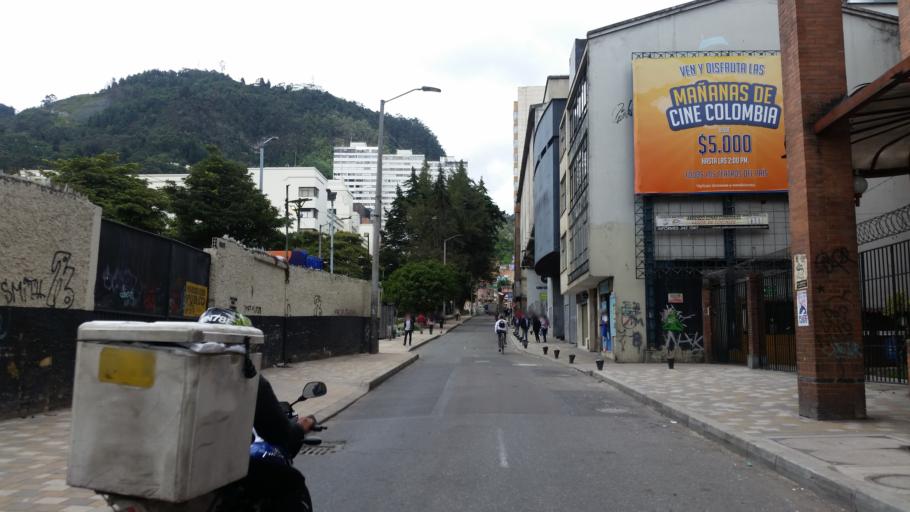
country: CO
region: Bogota D.C.
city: Bogota
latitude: 4.6098
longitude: -74.0698
